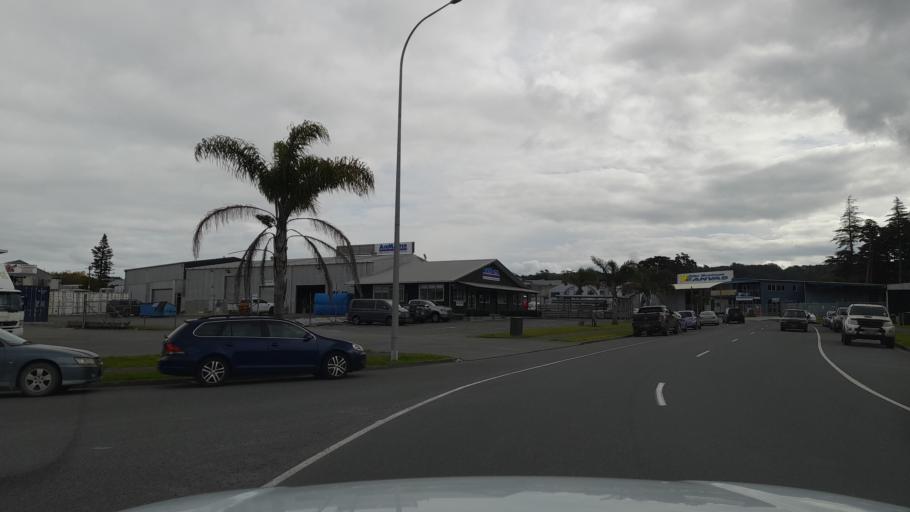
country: NZ
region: Northland
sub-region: Whangarei
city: Whangarei
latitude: -35.7498
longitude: 174.3130
